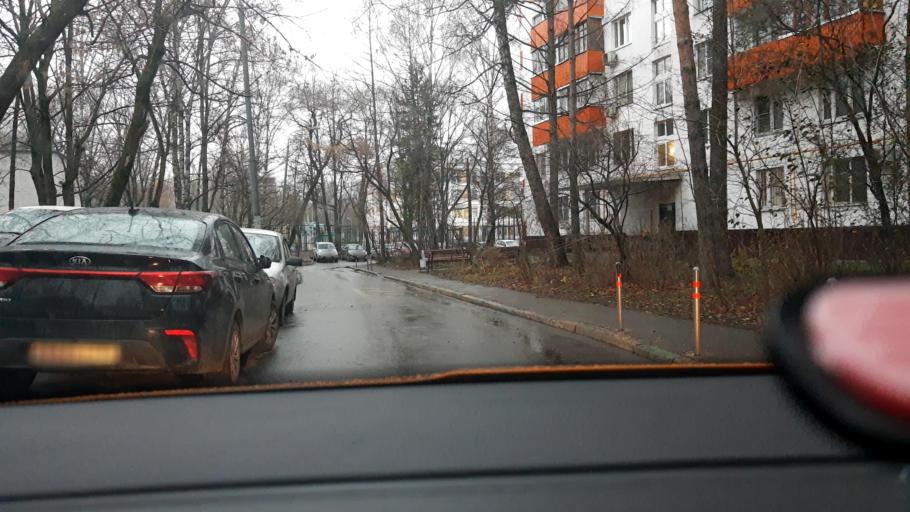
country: RU
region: Moscow
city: Strogino
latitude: 55.8516
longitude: 37.4114
